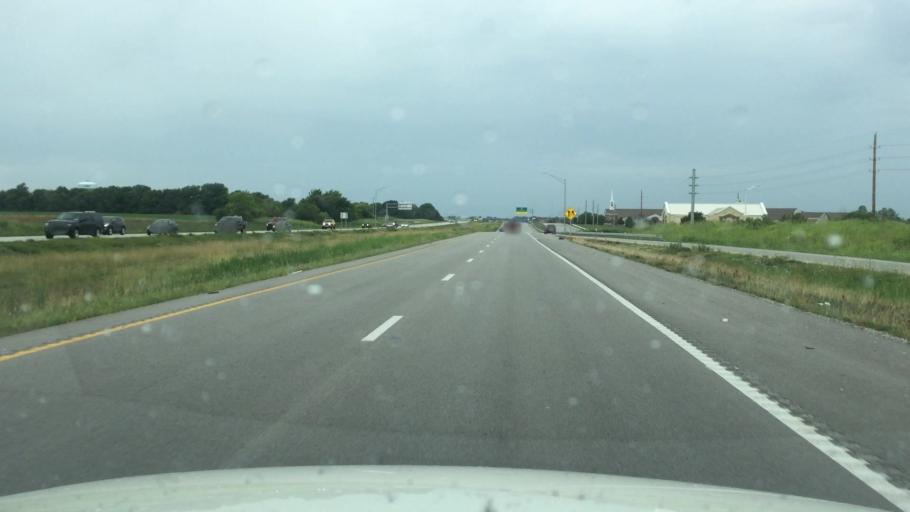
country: US
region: Missouri
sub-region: Jackson County
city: Greenwood
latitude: 38.9018
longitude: -94.3205
